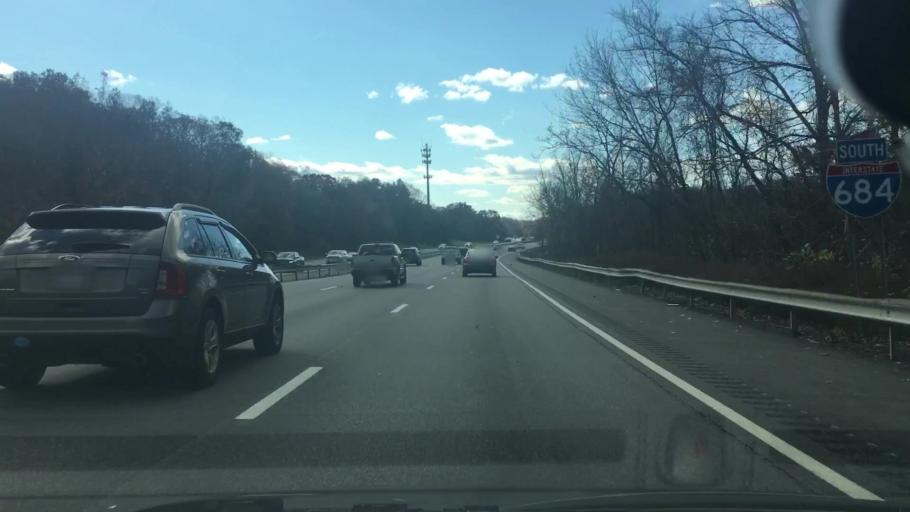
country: US
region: New York
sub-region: Westchester County
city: Goldens Bridge
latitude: 41.2874
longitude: -73.6782
